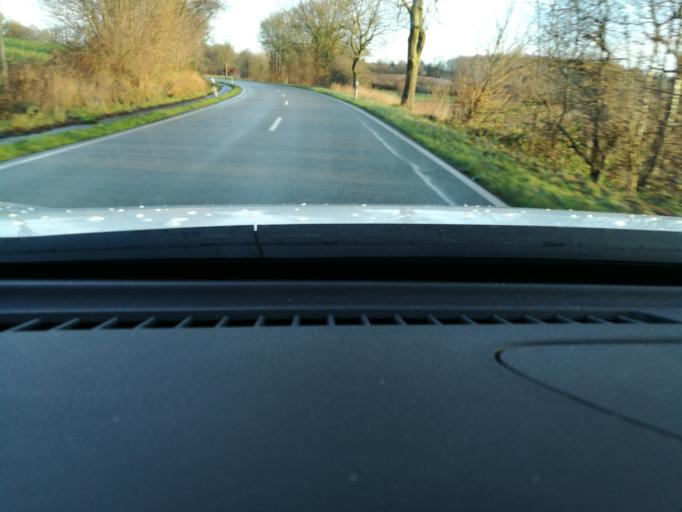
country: DE
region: Schleswig-Holstein
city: Ascheffel
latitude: 54.4143
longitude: 9.7019
